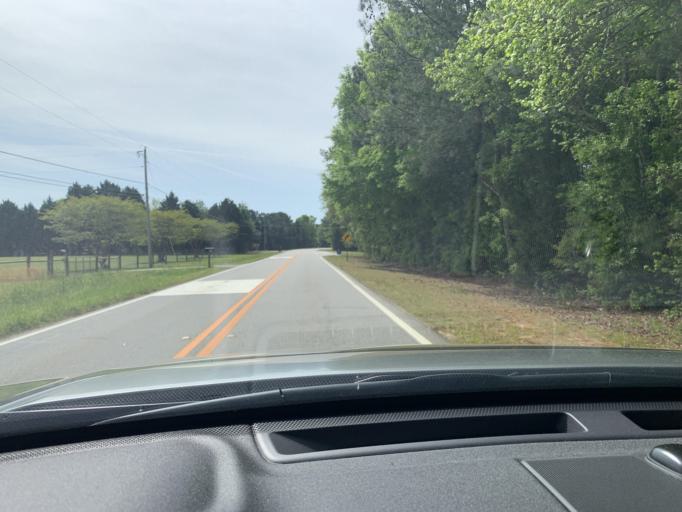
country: US
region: Georgia
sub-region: Oconee County
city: Watkinsville
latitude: 33.8418
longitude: -83.4468
